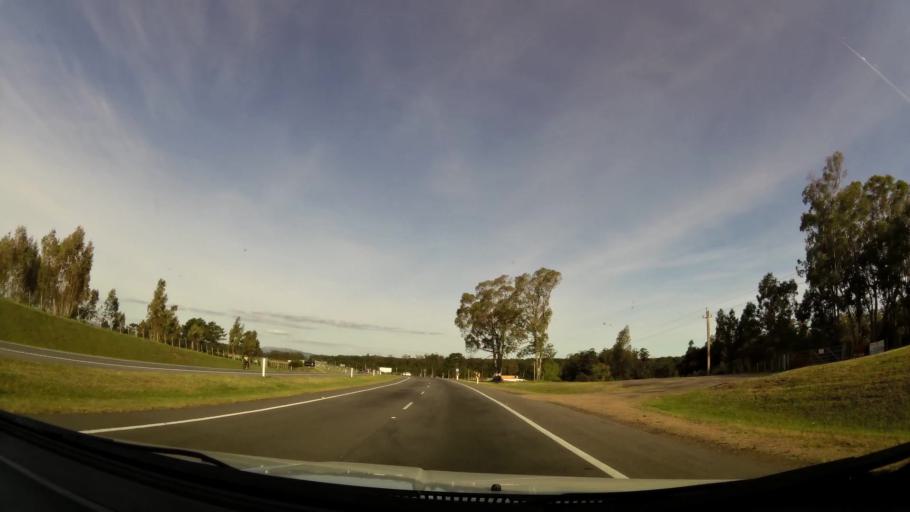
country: UY
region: Canelones
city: La Floresta
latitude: -34.7876
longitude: -55.5178
